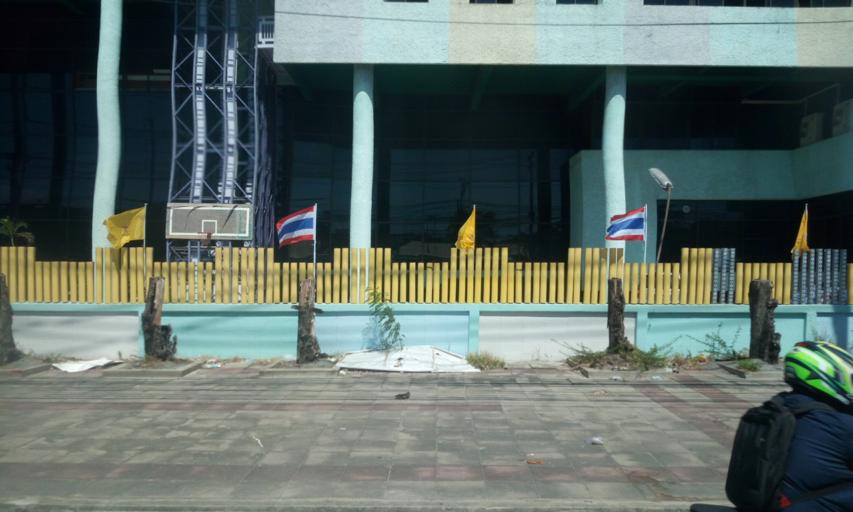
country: TH
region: Samut Prakan
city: Bang Bo District
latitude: 13.5744
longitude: 100.7943
